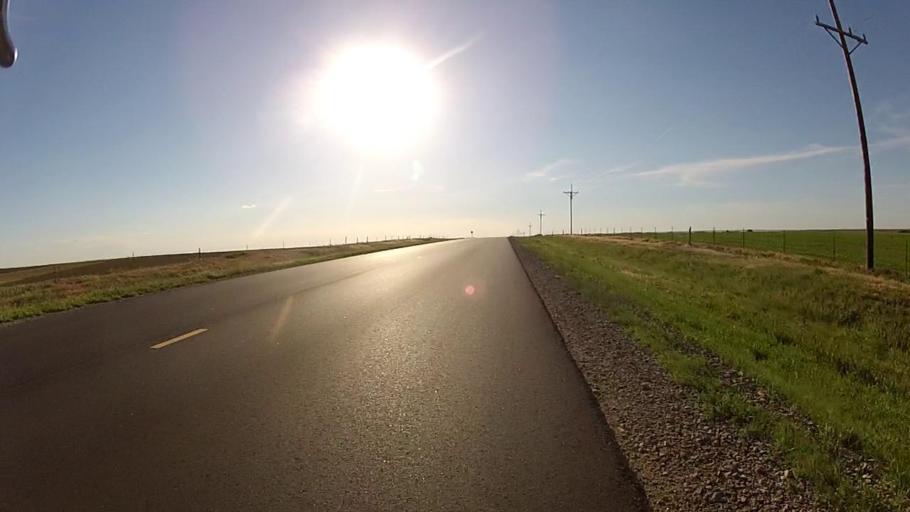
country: US
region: Kansas
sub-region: Comanche County
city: Coldwater
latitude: 37.2821
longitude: -99.1152
